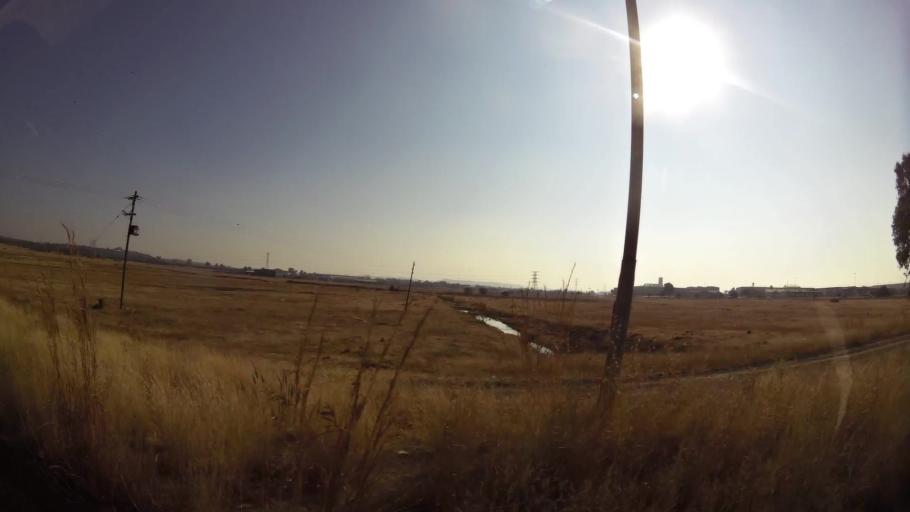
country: ZA
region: Orange Free State
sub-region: Mangaung Metropolitan Municipality
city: Bloemfontein
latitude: -29.1721
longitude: 26.2187
